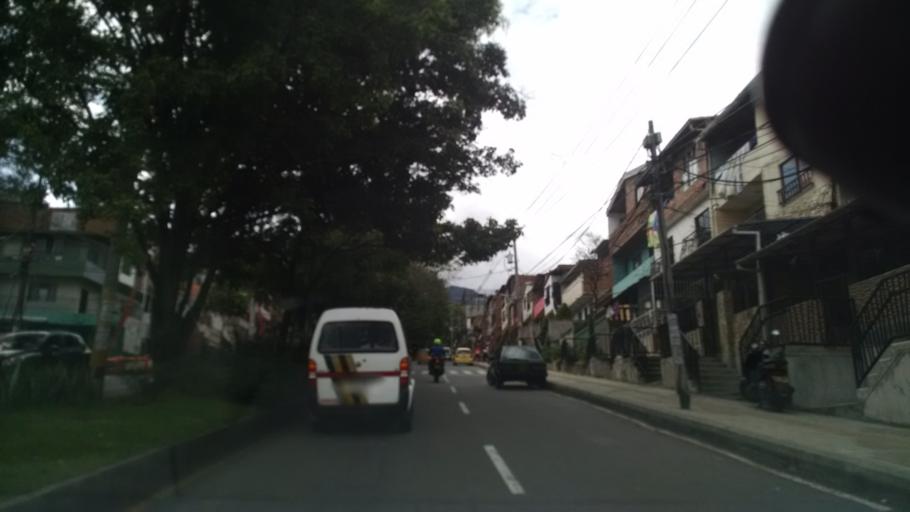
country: CO
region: Antioquia
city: Bello
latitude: 6.3004
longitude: -75.5702
